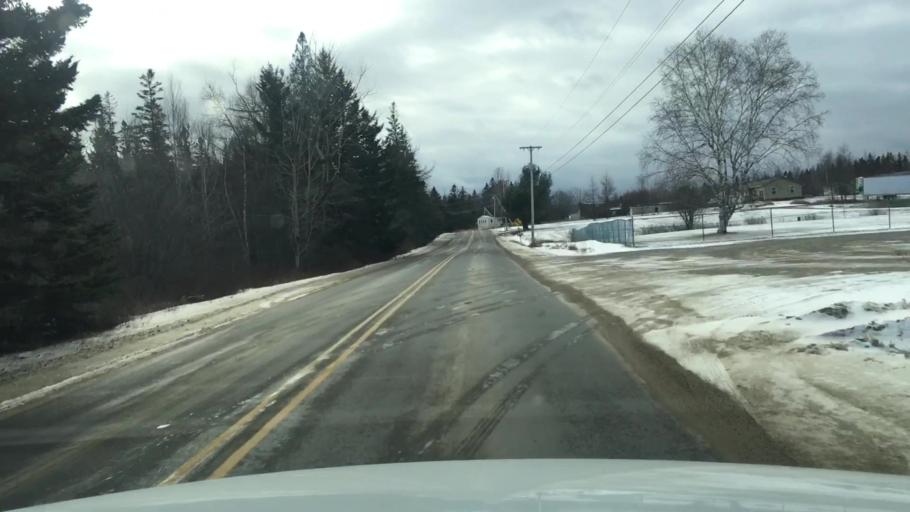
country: US
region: Maine
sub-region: Washington County
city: Jonesport
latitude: 44.6265
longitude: -67.5989
